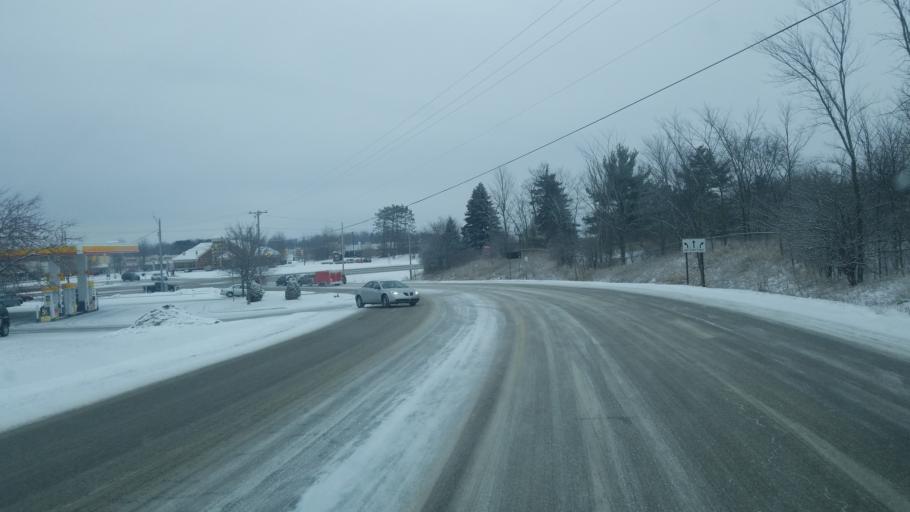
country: US
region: Michigan
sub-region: Mecosta County
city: Big Rapids
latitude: 43.6870
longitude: -85.5122
